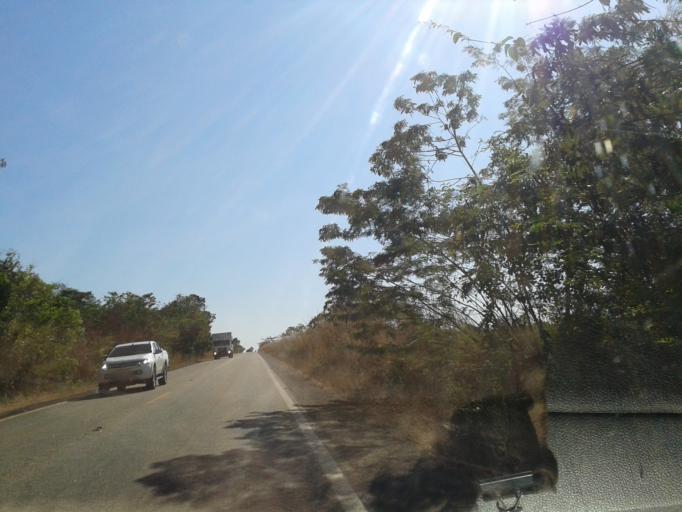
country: BR
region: Goias
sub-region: Mozarlandia
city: Mozarlandia
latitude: -14.5379
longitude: -50.4886
